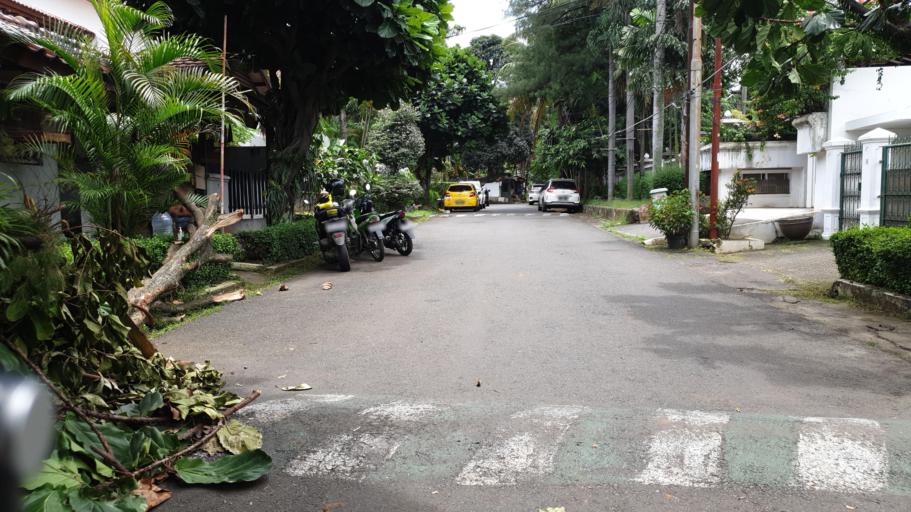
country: ID
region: West Java
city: Pamulang
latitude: -6.2973
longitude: 106.7809
